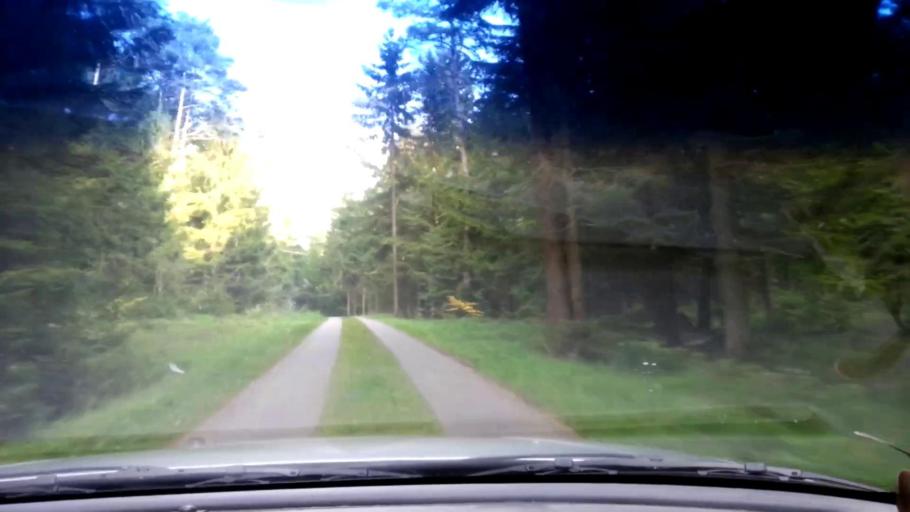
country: DE
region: Bavaria
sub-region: Upper Franconia
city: Wattendorf
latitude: 50.0041
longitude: 11.1108
